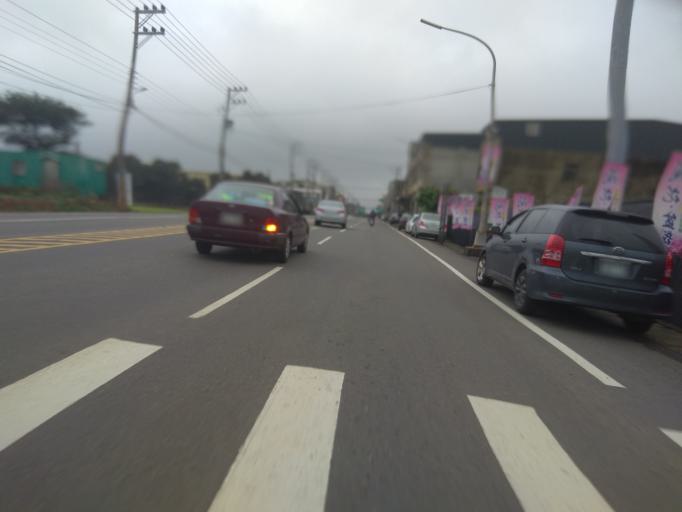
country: TW
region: Taiwan
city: Taoyuan City
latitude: 25.0290
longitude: 121.1070
